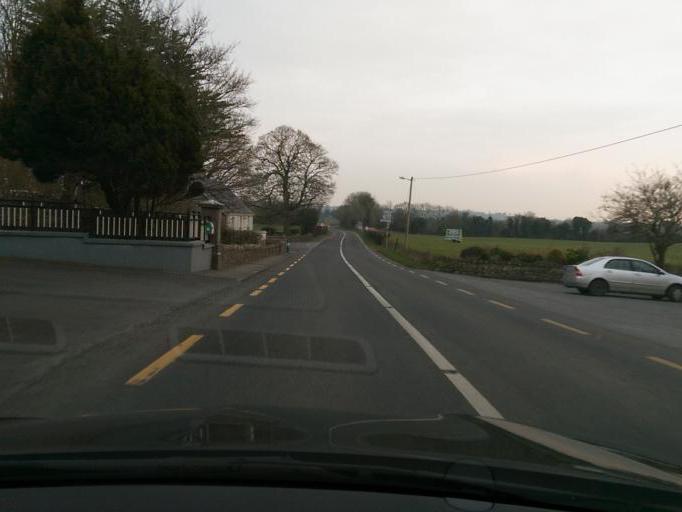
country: IE
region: Leinster
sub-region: An Longfort
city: Ballymahon
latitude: 53.5294
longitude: -7.7932
